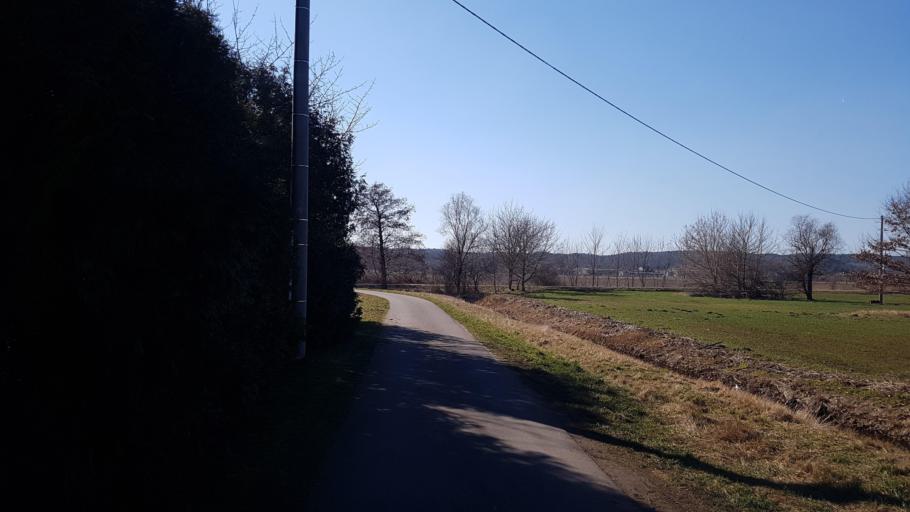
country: DE
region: Brandenburg
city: Hirschfeld
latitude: 51.3909
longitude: 13.6328
